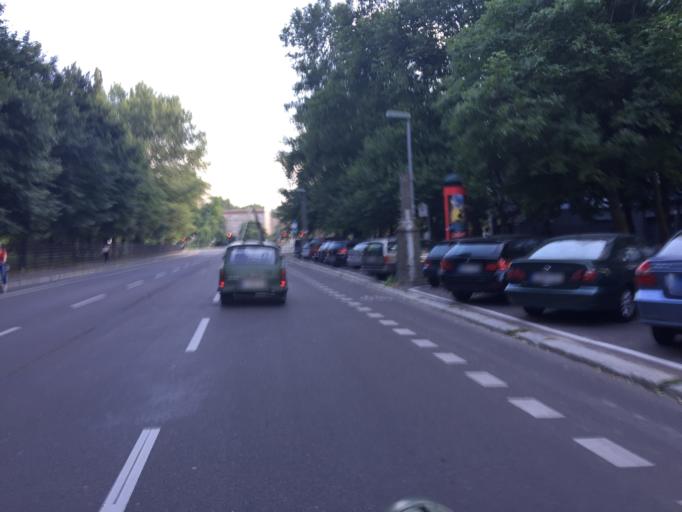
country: DE
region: Berlin
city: Friedrichshain Bezirk
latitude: 52.5151
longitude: 13.4401
